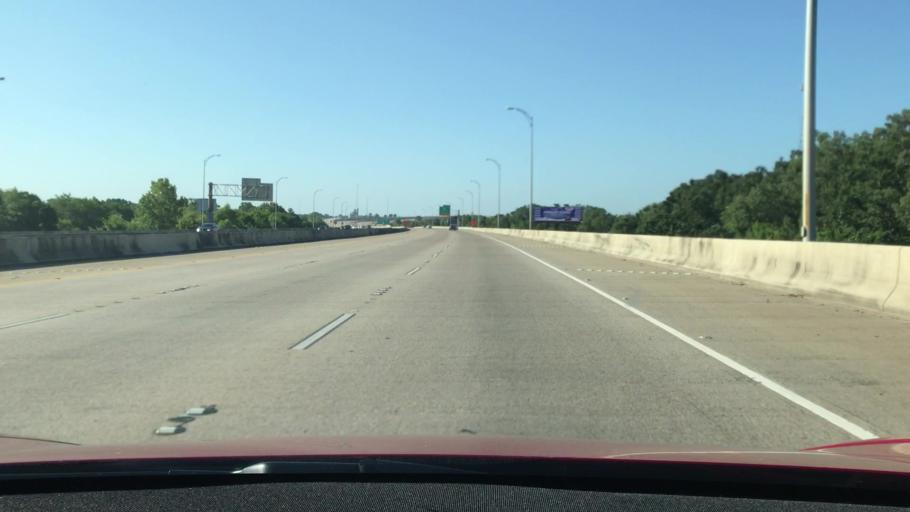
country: US
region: Louisiana
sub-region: Bossier Parish
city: Bossier City
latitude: 32.4328
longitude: -93.7549
